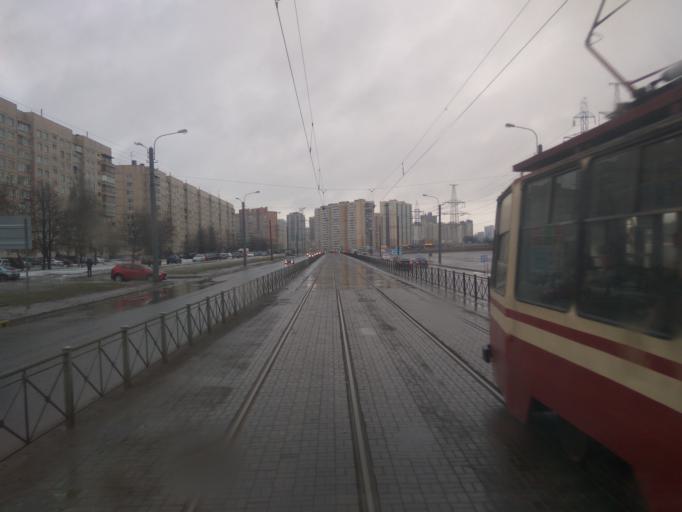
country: RU
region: St.-Petersburg
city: Uritsk
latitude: 59.8600
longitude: 30.2127
